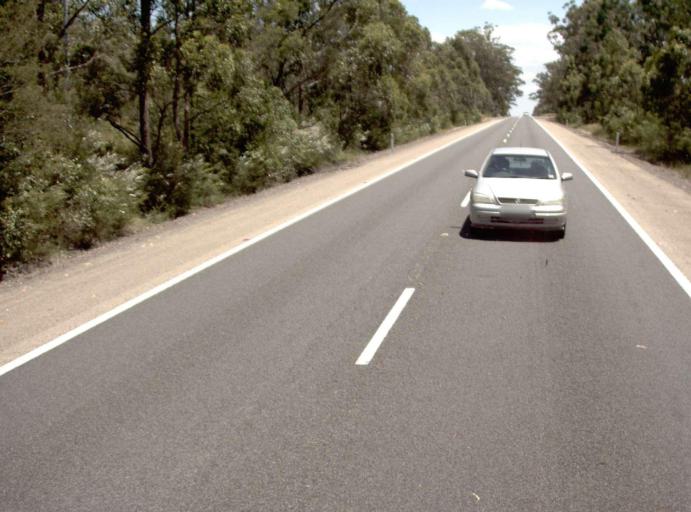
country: AU
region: Victoria
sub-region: East Gippsland
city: Lakes Entrance
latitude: -37.7536
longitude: 148.3271
